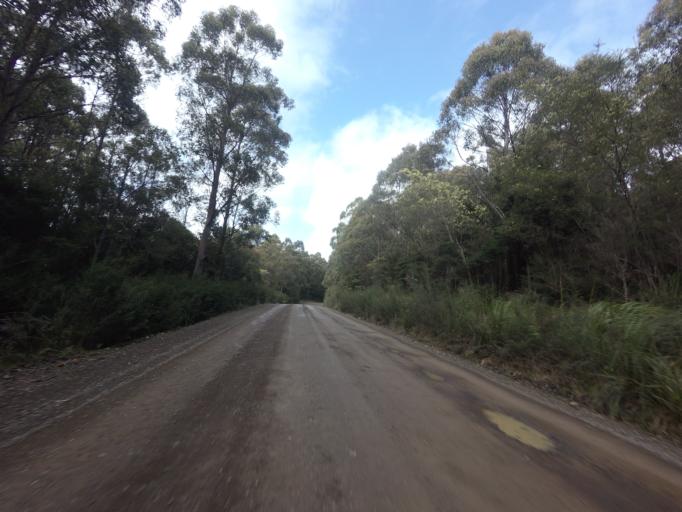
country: AU
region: Tasmania
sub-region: Huon Valley
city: Geeveston
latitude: -43.4642
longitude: 146.8999
